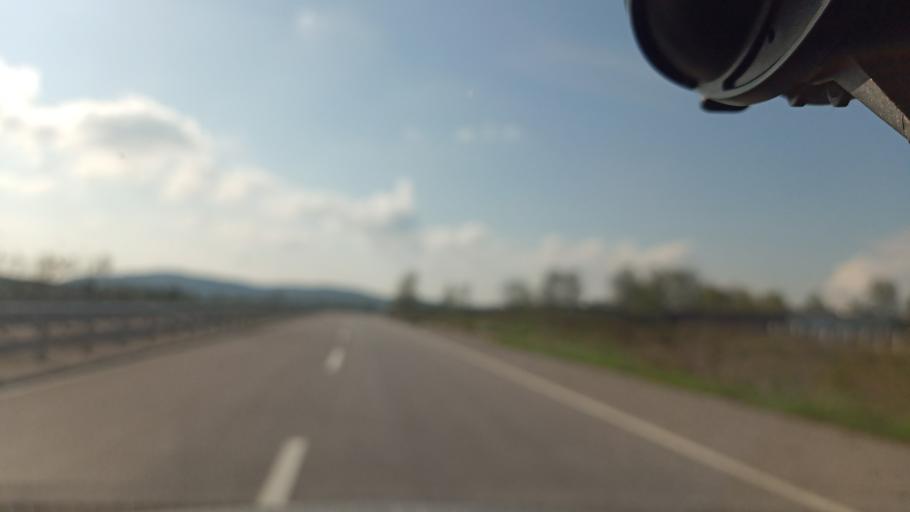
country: TR
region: Sakarya
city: Kaynarca
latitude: 41.0325
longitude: 30.3269
